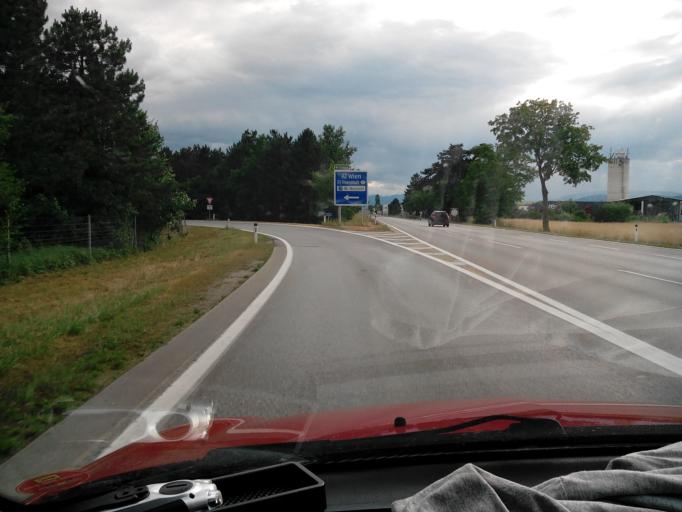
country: AT
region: Lower Austria
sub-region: Wiener Neustadt Stadt
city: Wiener Neustadt
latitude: 47.7848
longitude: 16.1991
